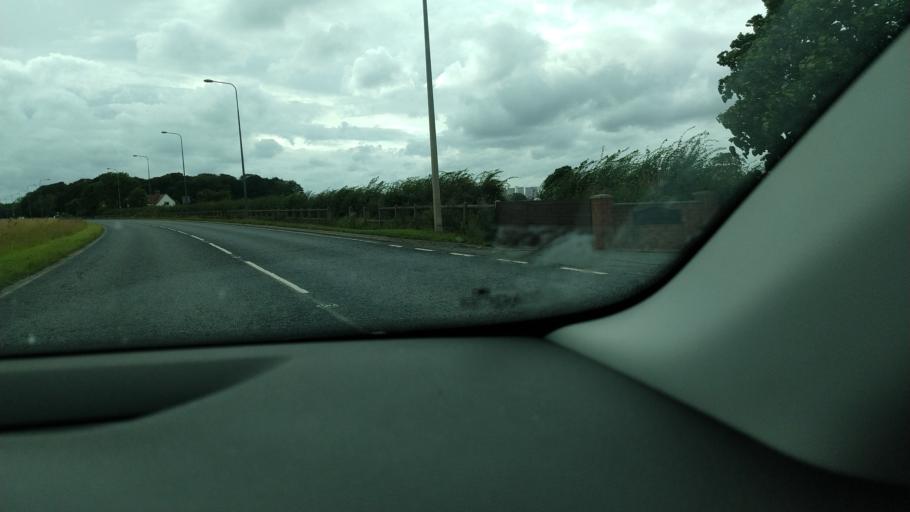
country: GB
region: England
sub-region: East Riding of Yorkshire
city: Airmyn
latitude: 53.7071
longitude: -0.9247
